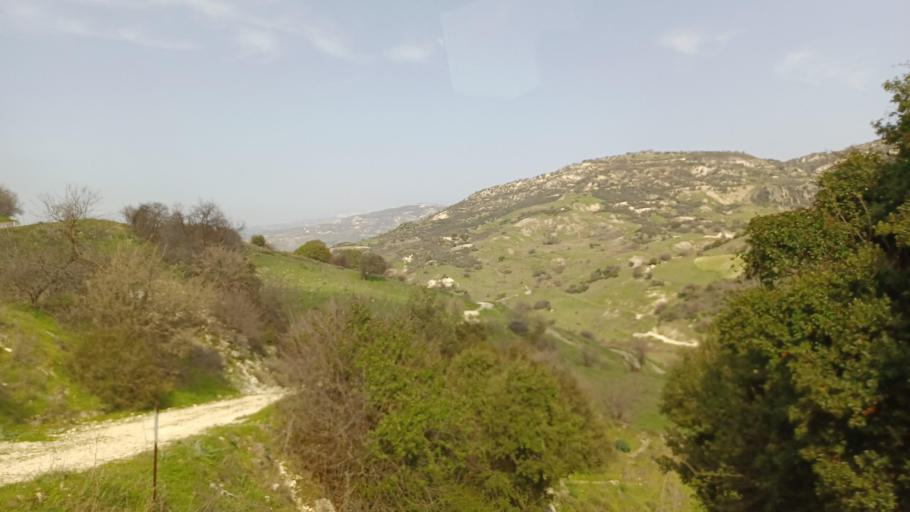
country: CY
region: Limassol
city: Pissouri
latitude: 34.7492
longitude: 32.6602
